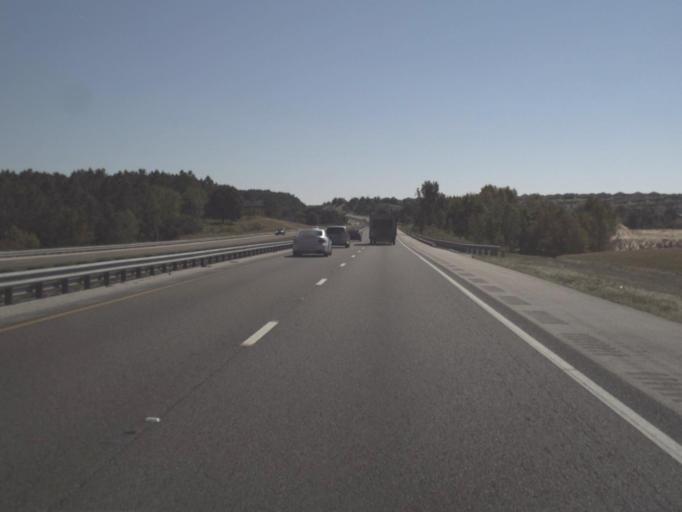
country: US
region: Florida
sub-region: Lake County
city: Montverde
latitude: 28.5810
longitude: -81.7043
